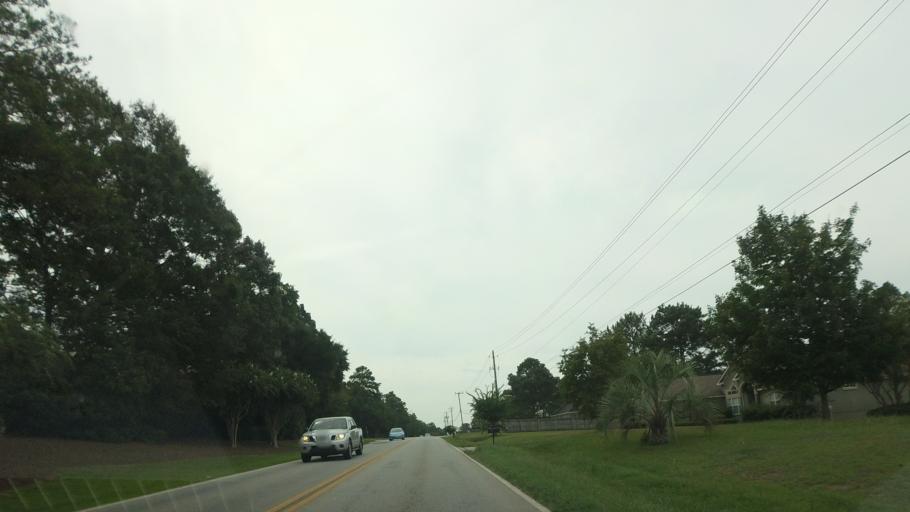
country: US
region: Georgia
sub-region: Houston County
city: Robins Air Force Base
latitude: 32.5717
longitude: -83.5891
